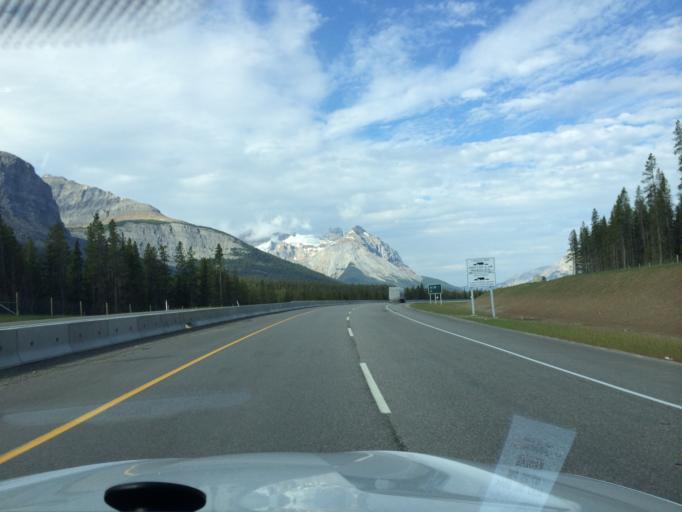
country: CA
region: Alberta
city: Lake Louise
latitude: 51.4547
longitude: -116.2791
